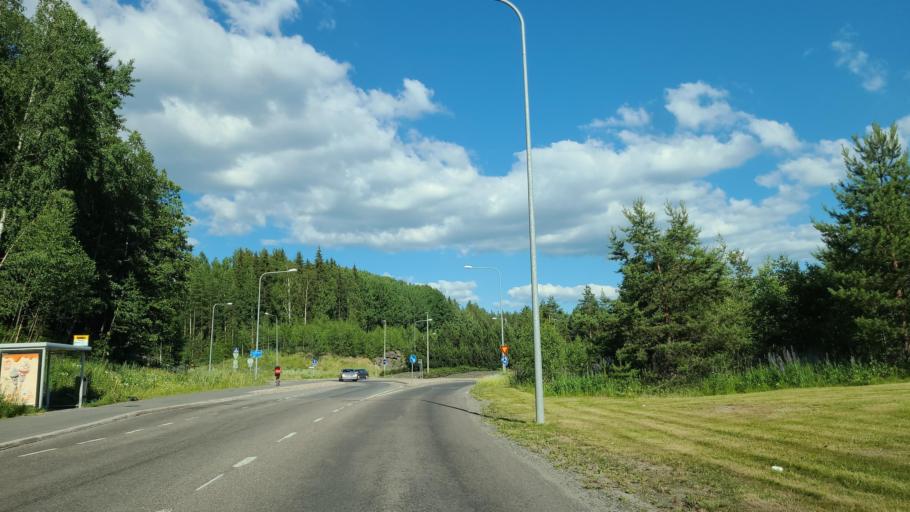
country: FI
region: Central Finland
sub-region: Jyvaeskylae
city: Jyvaeskylae
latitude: 62.2412
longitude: 25.8104
